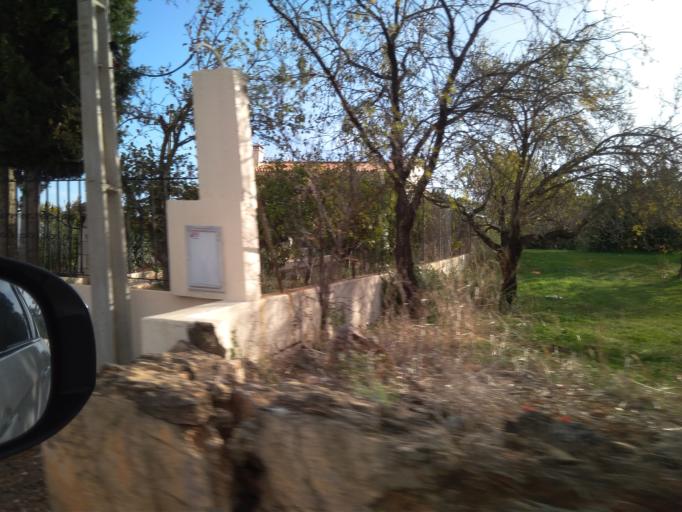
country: PT
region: Faro
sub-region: Faro
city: Santa Barbara de Nexe
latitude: 37.0934
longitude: -7.9437
